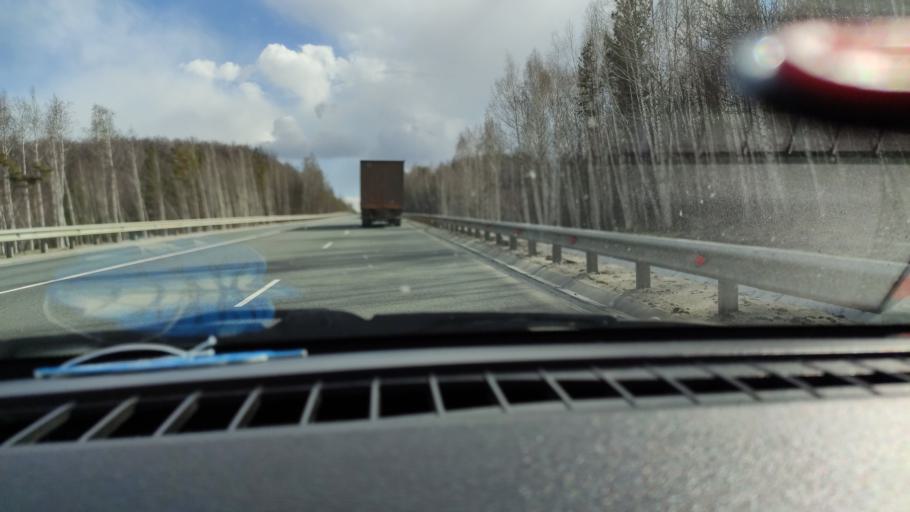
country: RU
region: Saratov
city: Khvalynsk
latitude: 52.4967
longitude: 48.0145
